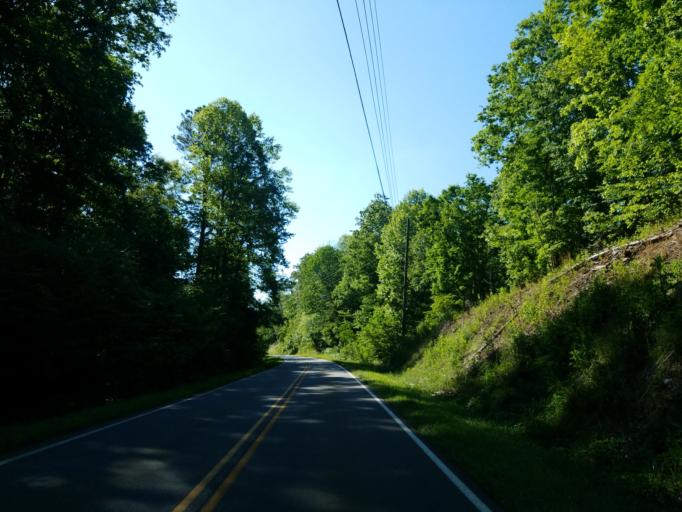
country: US
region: Georgia
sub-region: Pickens County
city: Jasper
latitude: 34.5191
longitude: -84.5050
